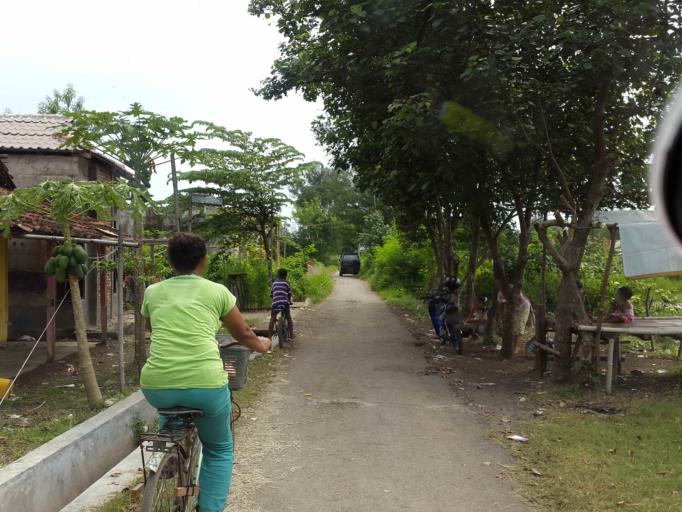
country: ID
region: Central Java
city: Pemalang
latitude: -6.8641
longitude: 109.3669
